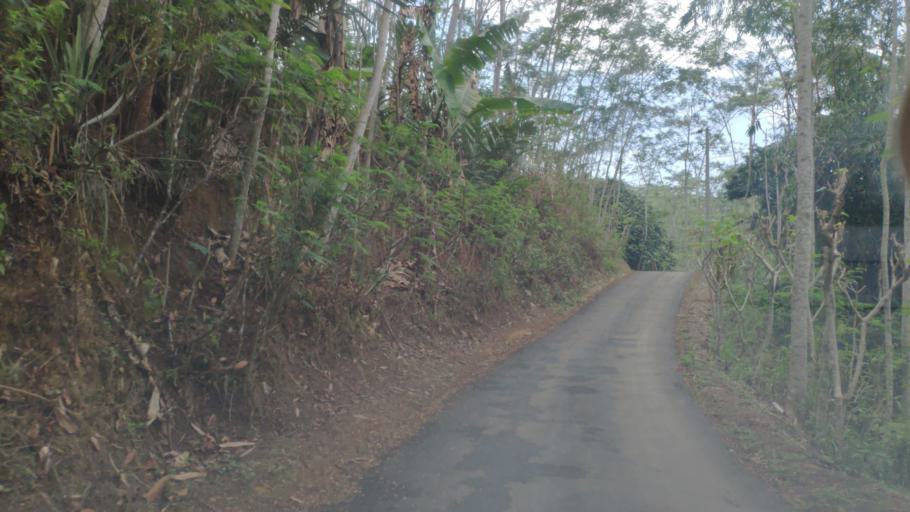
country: ID
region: Central Java
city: Wonosobo
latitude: -7.4422
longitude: 109.8269
